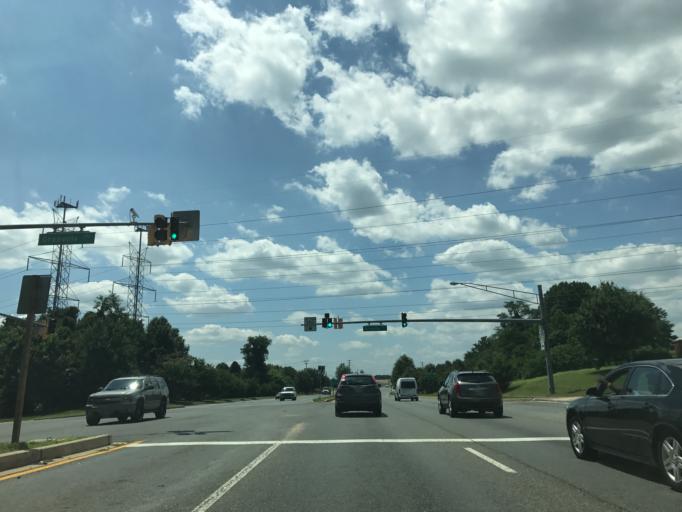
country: US
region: Maryland
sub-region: Prince George's County
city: Bowie
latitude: 38.9724
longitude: -76.7673
